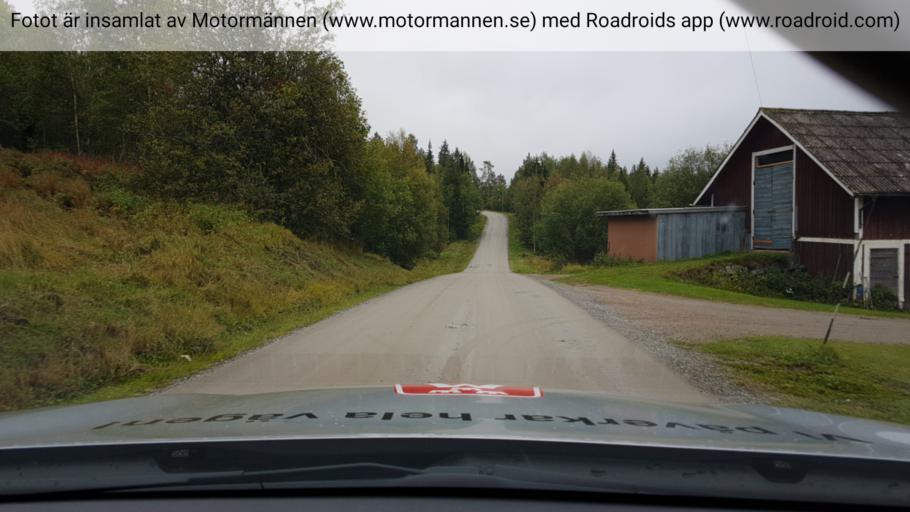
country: SE
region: Jaemtland
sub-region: Braecke Kommun
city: Braecke
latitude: 62.7710
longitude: 15.4844
